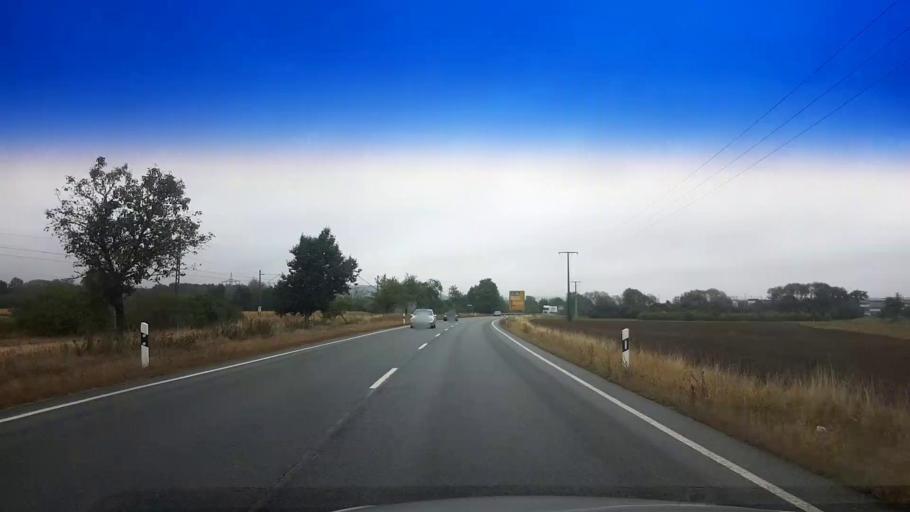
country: DE
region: Bavaria
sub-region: Upper Franconia
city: Eggolsheim
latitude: 49.7583
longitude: 11.0513
